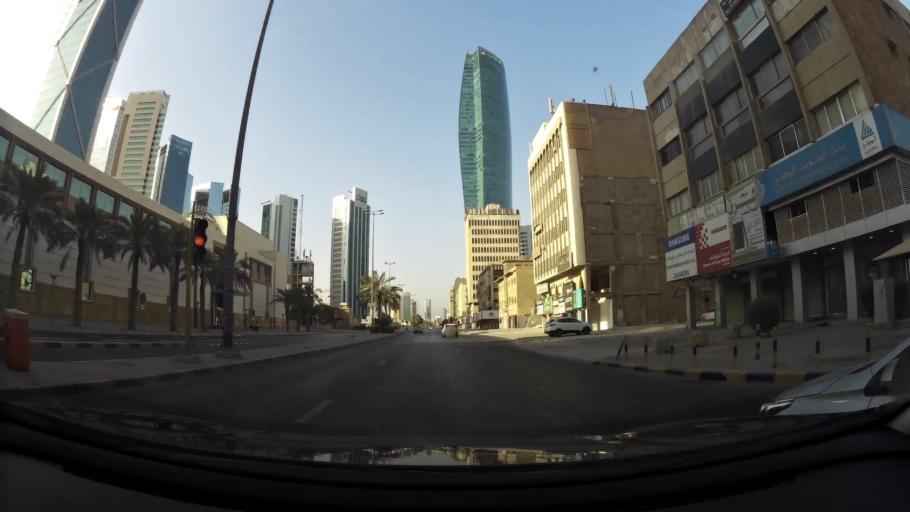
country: KW
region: Al Asimah
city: Kuwait City
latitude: 29.3778
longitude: 47.9902
